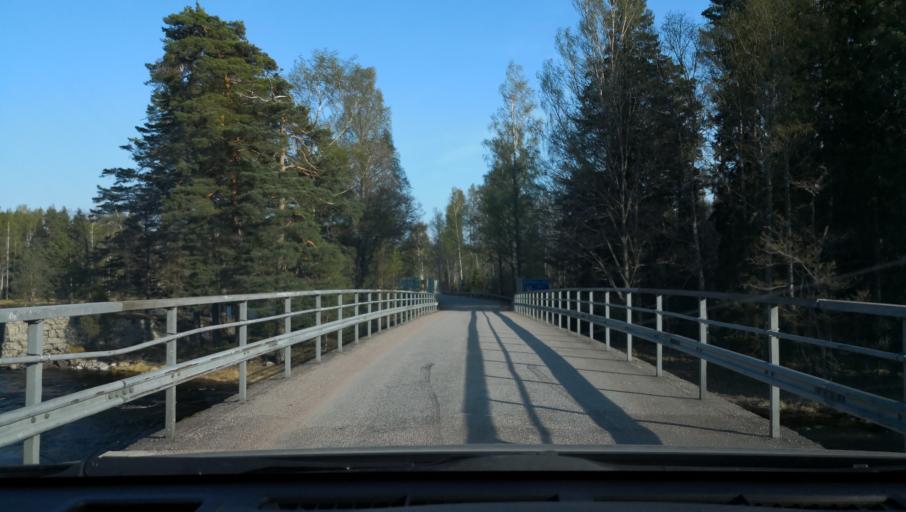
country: SE
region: Uppsala
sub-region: Heby Kommun
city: Tarnsjo
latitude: 60.2695
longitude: 16.9098
